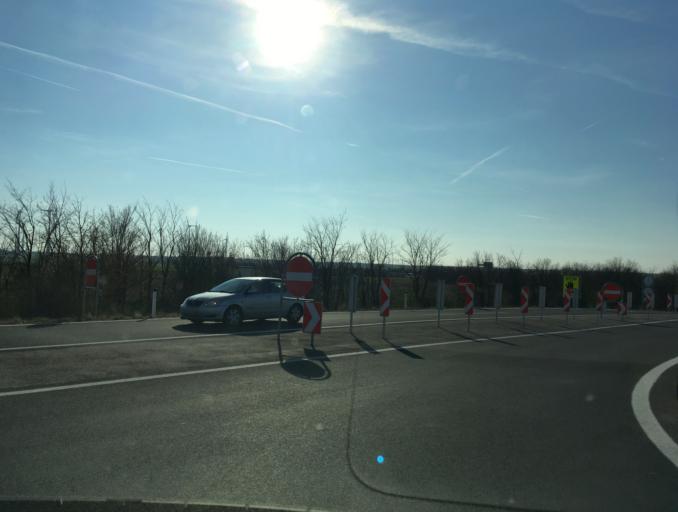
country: AT
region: Burgenland
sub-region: Politischer Bezirk Neusiedl am See
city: Nickelsdorf
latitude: 47.9271
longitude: 17.0928
